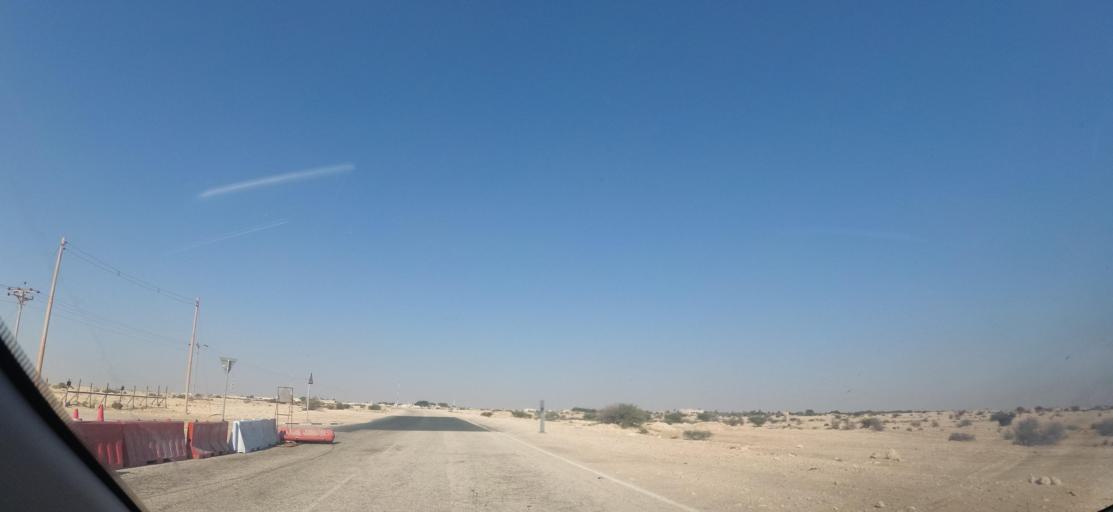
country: QA
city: Al Jumayliyah
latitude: 25.6062
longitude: 51.0761
